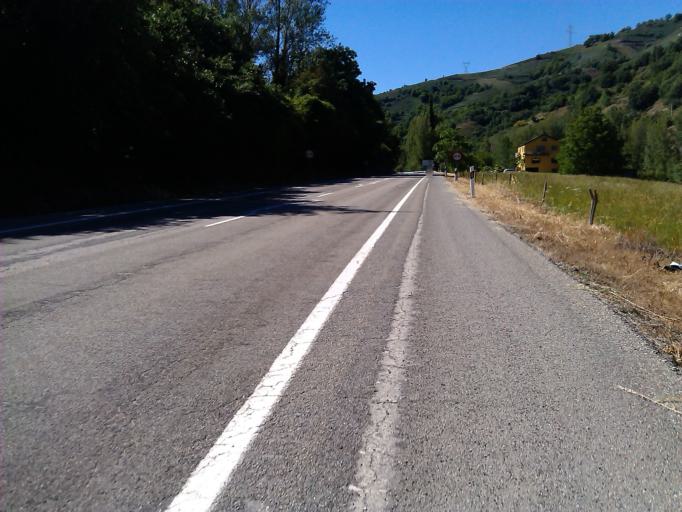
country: ES
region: Castille and Leon
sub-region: Provincia de Leon
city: Trabadelo
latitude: 42.6432
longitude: -6.8717
